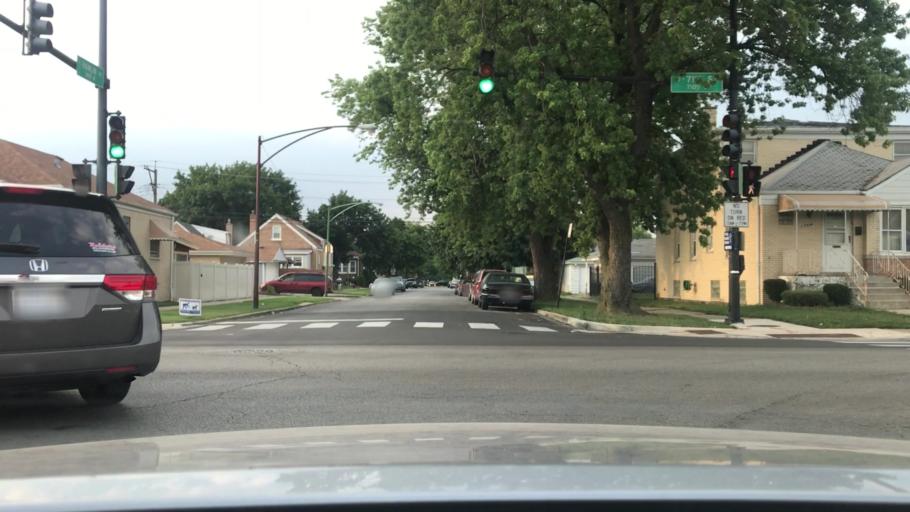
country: US
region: Illinois
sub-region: Cook County
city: Hometown
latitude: 41.7641
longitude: -87.7175
